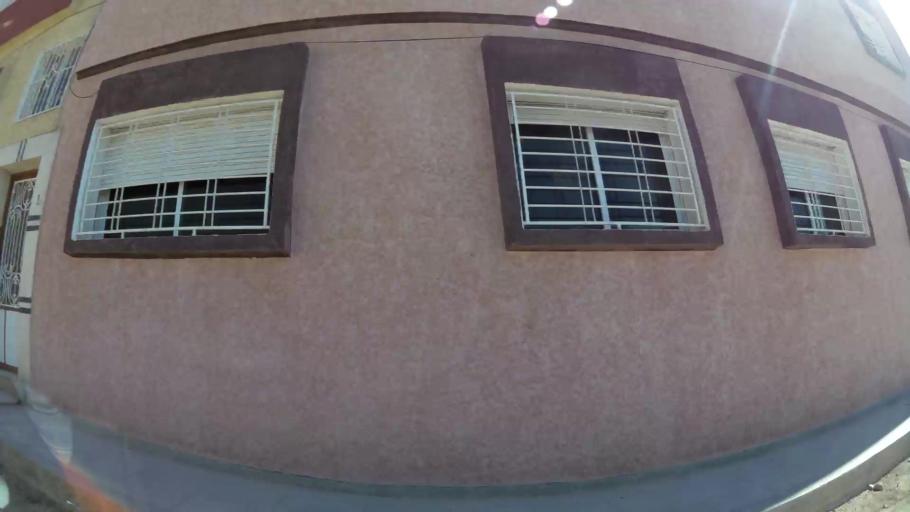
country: MA
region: Fes-Boulemane
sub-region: Fes
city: Fes
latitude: 33.9987
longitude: -5.0081
